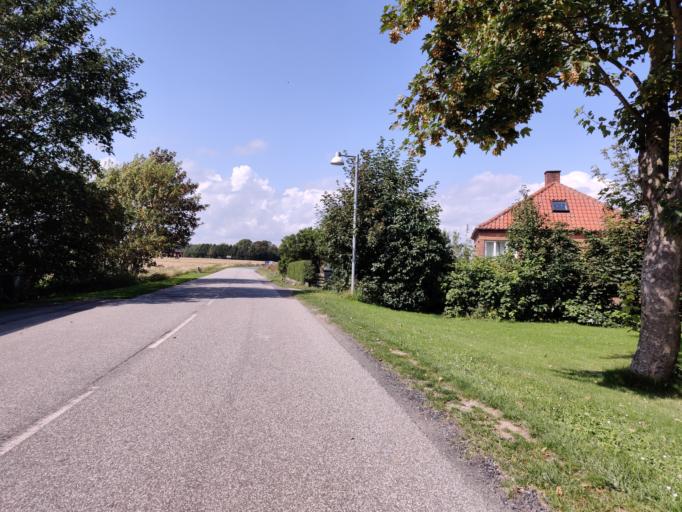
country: DK
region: Zealand
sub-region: Guldborgsund Kommune
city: Nykobing Falster
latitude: 54.6361
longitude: 11.9009
